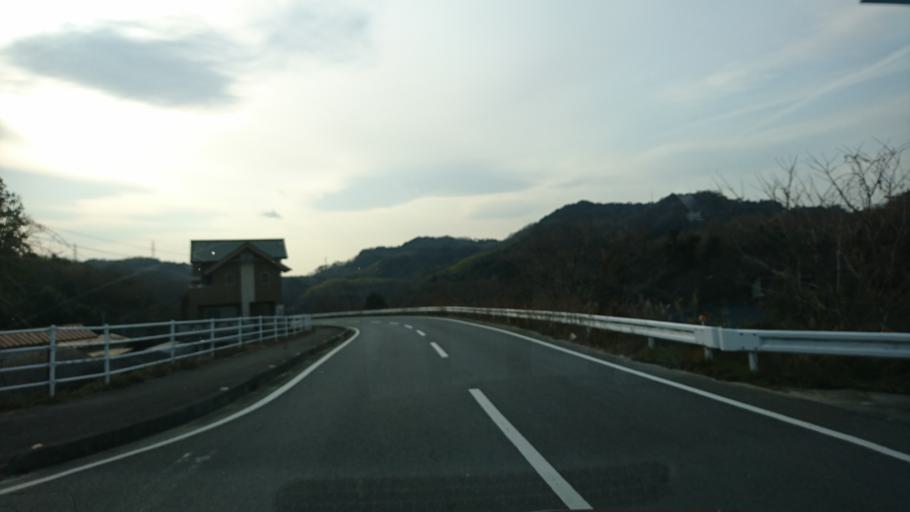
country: JP
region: Ehime
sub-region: Shikoku-chuo Shi
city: Matsuyama
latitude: 33.8904
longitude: 132.8033
